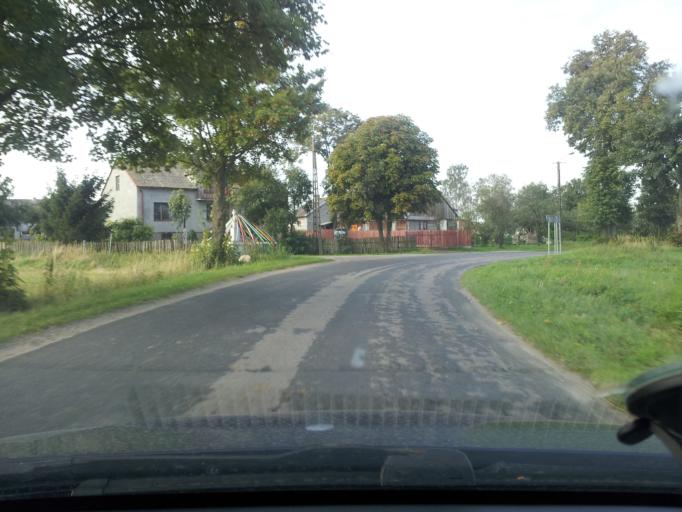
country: PL
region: Kujawsko-Pomorskie
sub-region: Powiat brodnicki
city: Swiedziebnia
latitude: 53.1467
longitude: 19.4948
